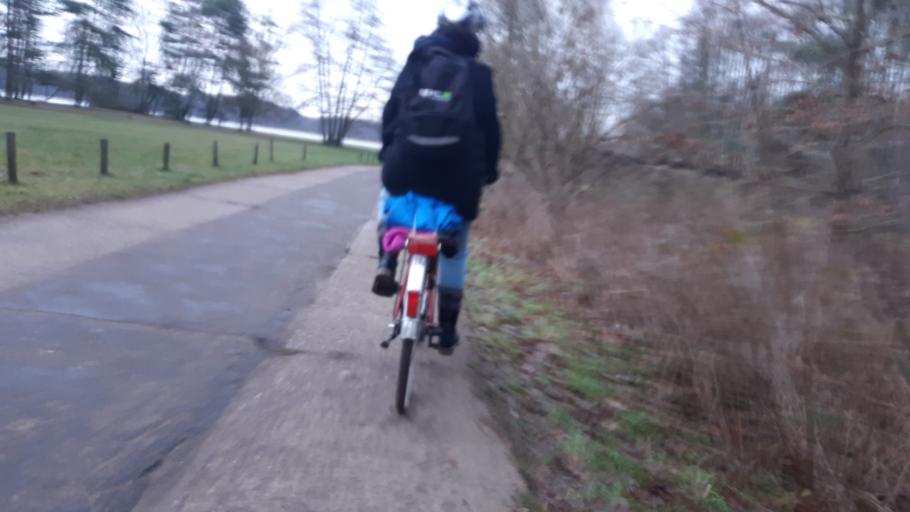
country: DE
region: Brandenburg
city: Templin
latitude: 53.1089
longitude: 13.5361
